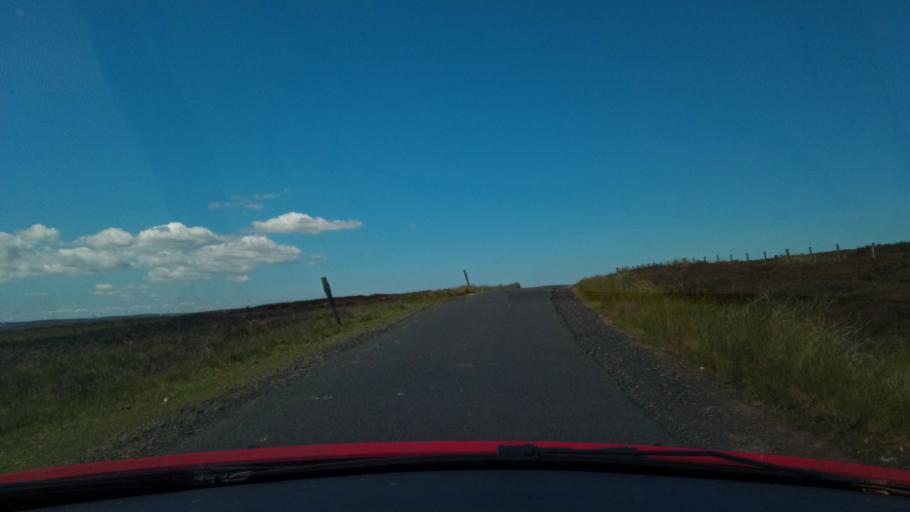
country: GB
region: Scotland
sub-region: East Lothian
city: Dunbar
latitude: 55.8344
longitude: -2.5412
